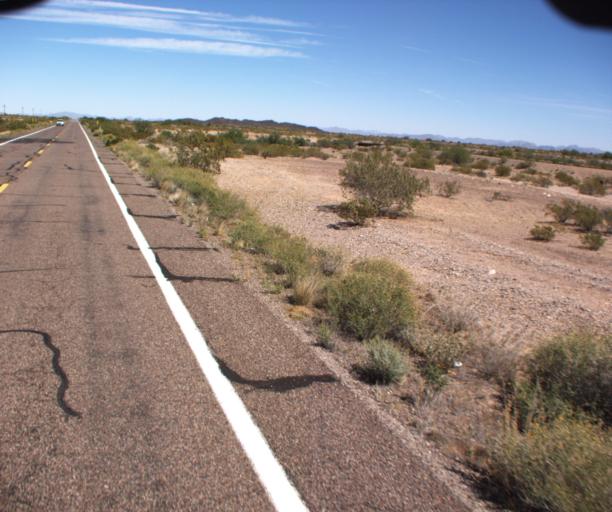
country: US
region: Arizona
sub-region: Maricopa County
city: Gila Bend
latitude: 32.7885
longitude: -112.8060
